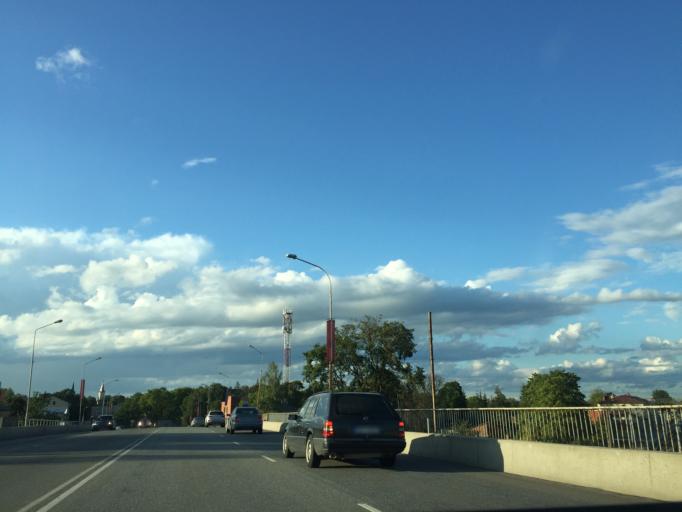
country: LV
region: Jelgava
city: Jelgava
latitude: 56.6388
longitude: 23.7290
